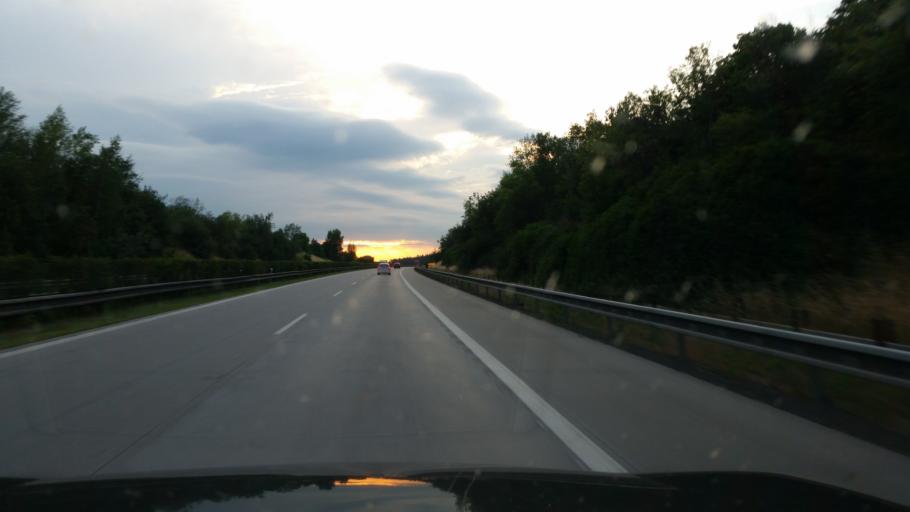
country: CZ
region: Olomoucky
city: Velky Ujezd
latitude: 49.5743
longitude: 17.4751
